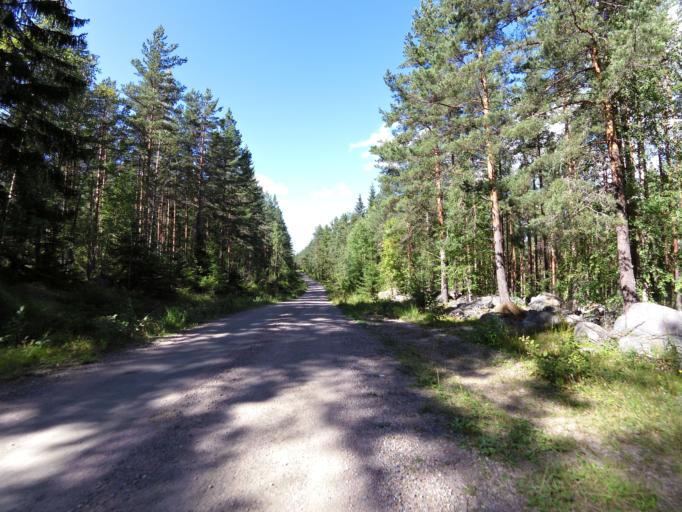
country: SE
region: Gaevleborg
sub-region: Gavle Kommun
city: Valbo
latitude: 60.7849
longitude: 16.9022
